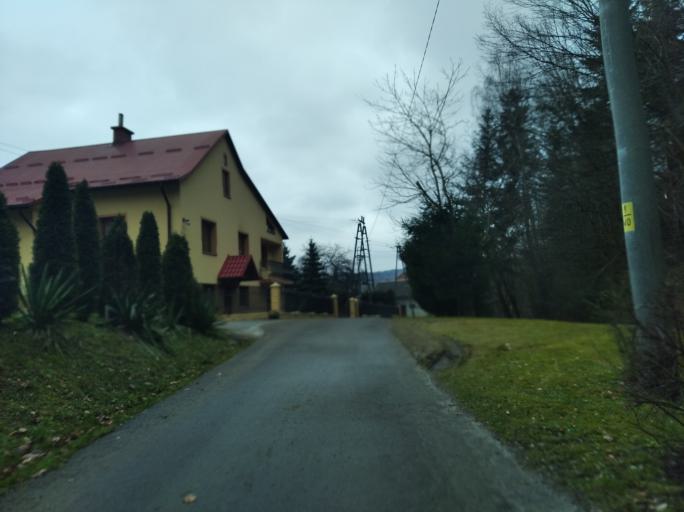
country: PL
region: Subcarpathian Voivodeship
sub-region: Powiat strzyzowski
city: Strzyzow
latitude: 49.8999
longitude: 21.8213
